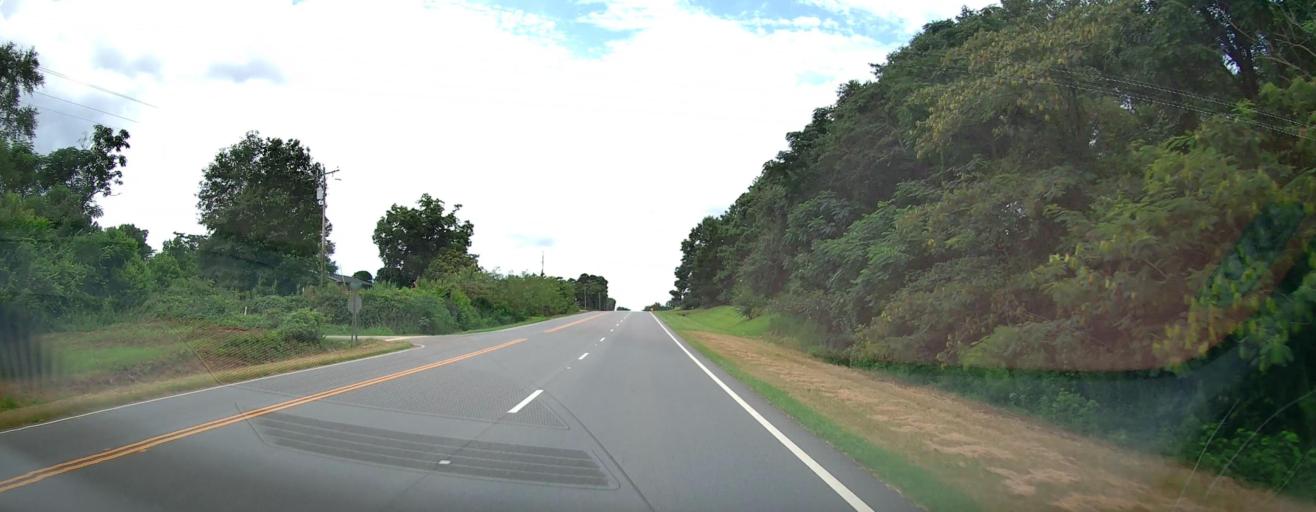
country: US
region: Georgia
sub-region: Macon County
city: Montezuma
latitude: 32.2930
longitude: -83.9500
